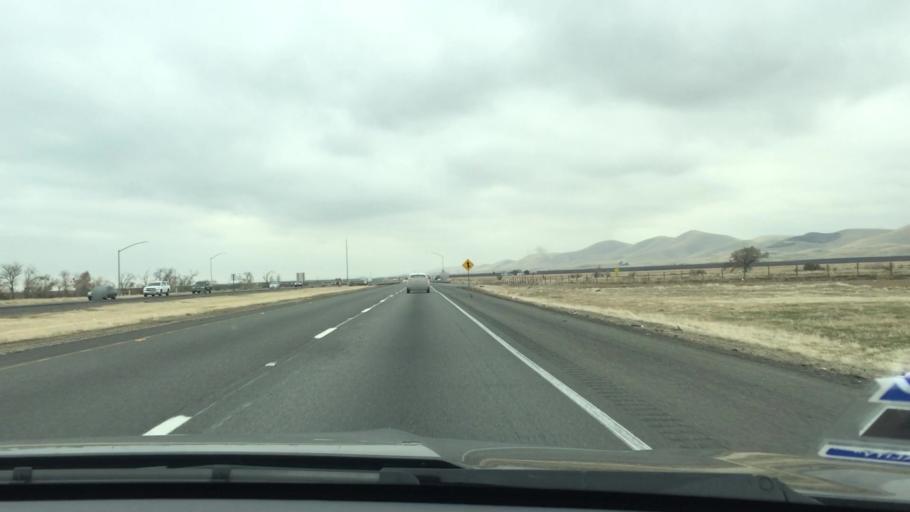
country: US
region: California
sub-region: Merced County
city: Gustine
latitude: 37.2455
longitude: -121.0890
